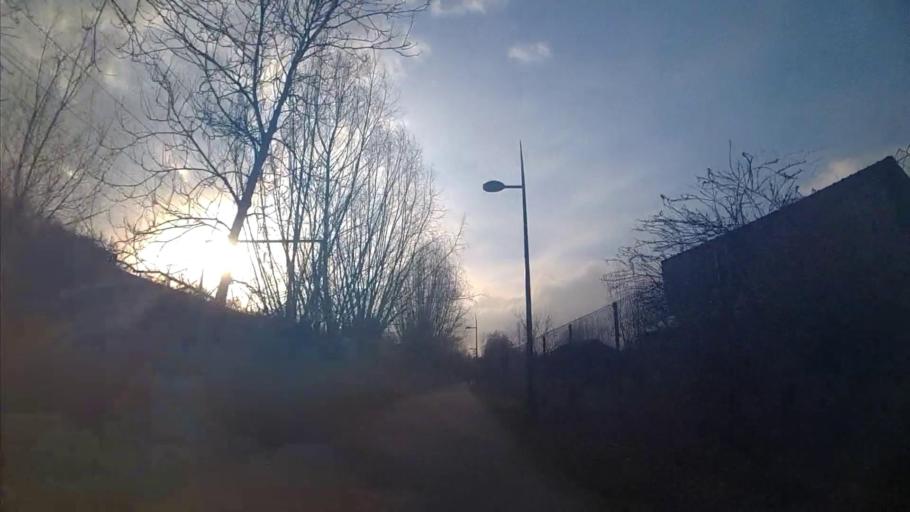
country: BE
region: Flanders
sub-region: Provincie Oost-Vlaanderen
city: Destelbergen
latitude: 51.0687
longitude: 3.7836
